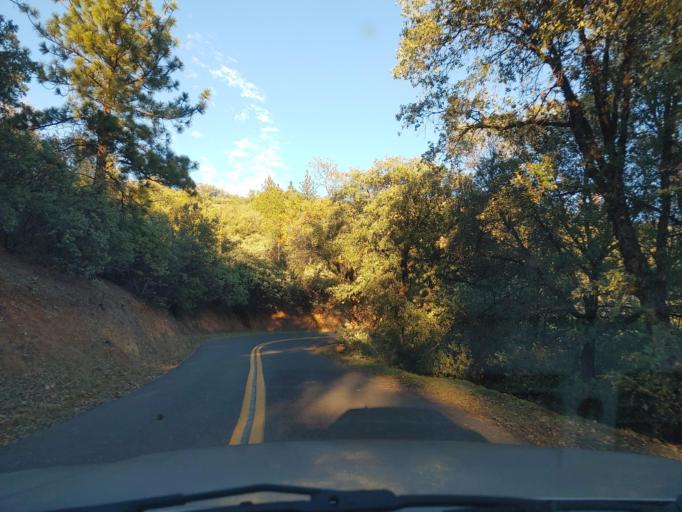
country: US
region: California
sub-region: Tuolumne County
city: Columbia
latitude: 38.0386
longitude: -120.3690
